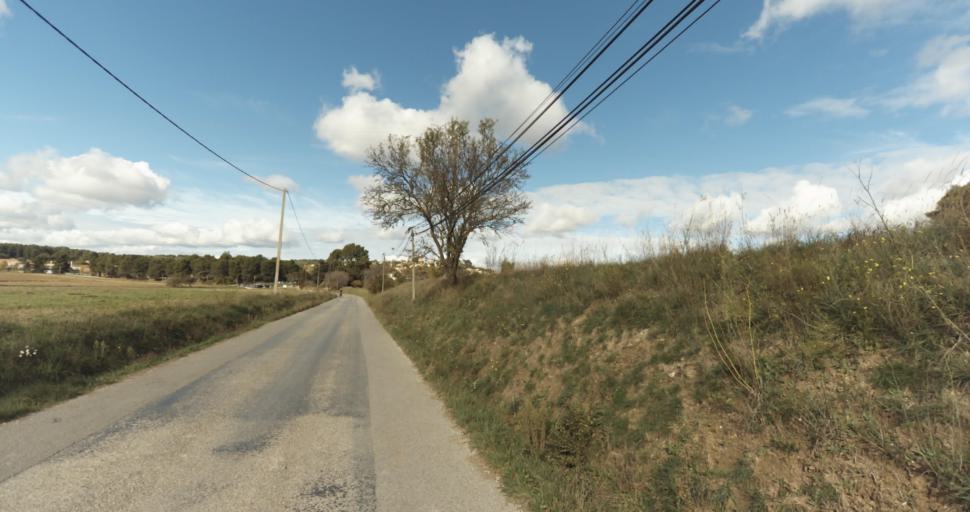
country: FR
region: Provence-Alpes-Cote d'Azur
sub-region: Departement des Bouches-du-Rhone
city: Venelles
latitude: 43.5899
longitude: 5.4873
